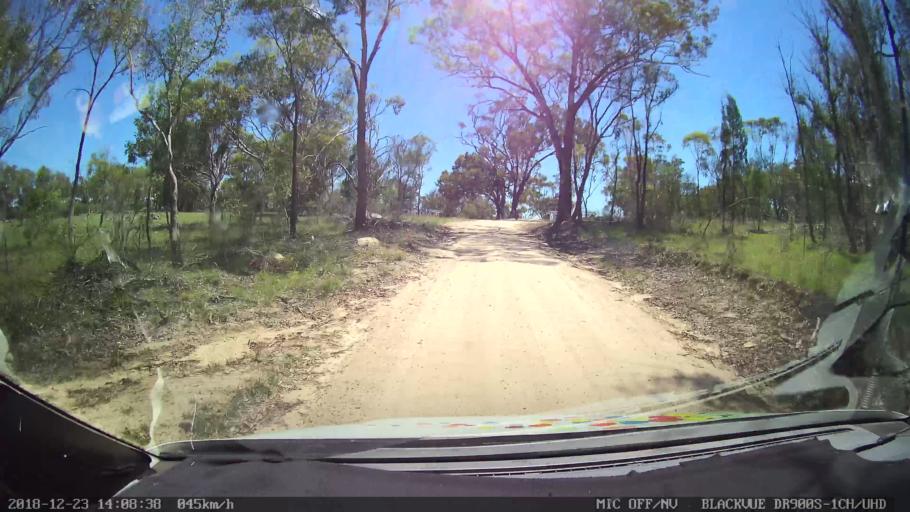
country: AU
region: New South Wales
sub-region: Tamworth Municipality
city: Manilla
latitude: -30.6429
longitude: 151.0667
